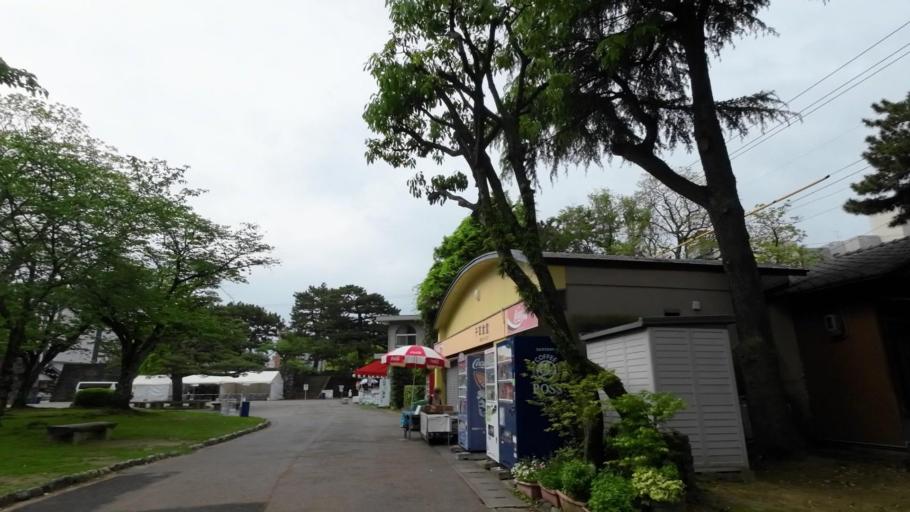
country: JP
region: Tokushima
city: Tokushima-shi
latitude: 34.0729
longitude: 134.5554
